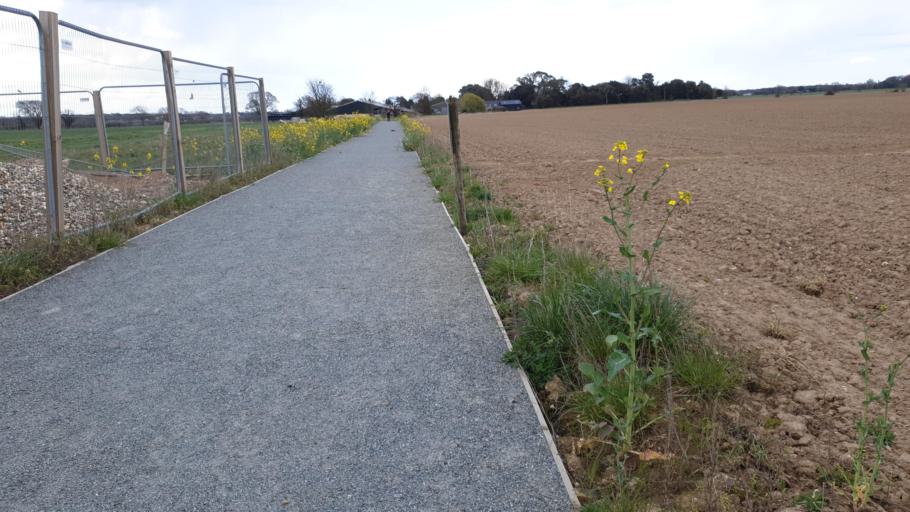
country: GB
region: England
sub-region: Essex
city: Great Bentley
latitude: 51.8491
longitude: 1.0696
